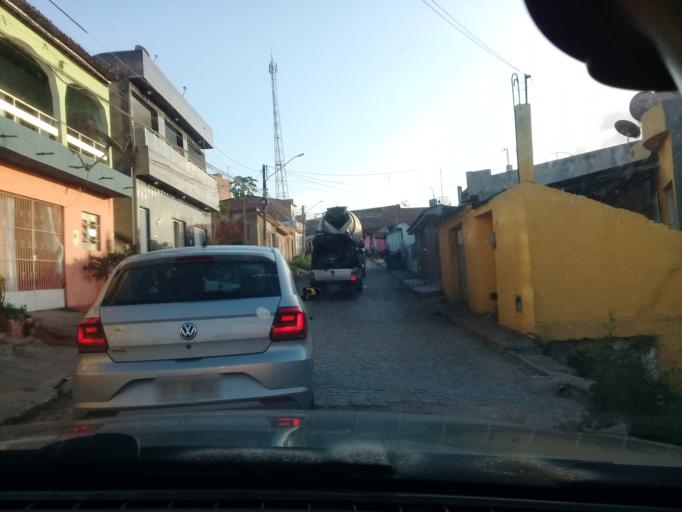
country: BR
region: Pernambuco
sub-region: Vitoria De Santo Antao
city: Vitoria de Santo Antao
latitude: -8.1286
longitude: -35.2860
